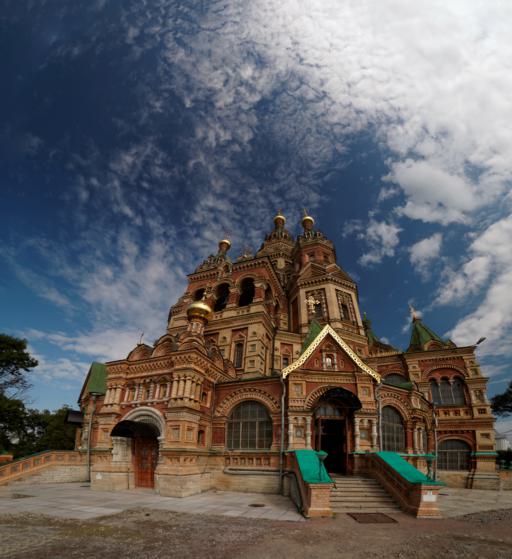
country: RU
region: St.-Petersburg
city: Peterhof
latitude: 59.8789
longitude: 29.9121
